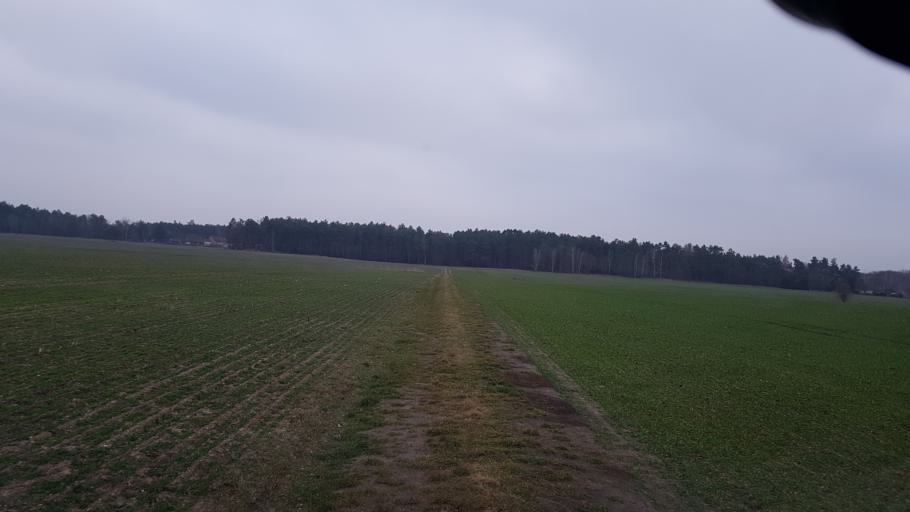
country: DE
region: Brandenburg
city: Schonewalde
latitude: 51.6421
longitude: 13.6176
